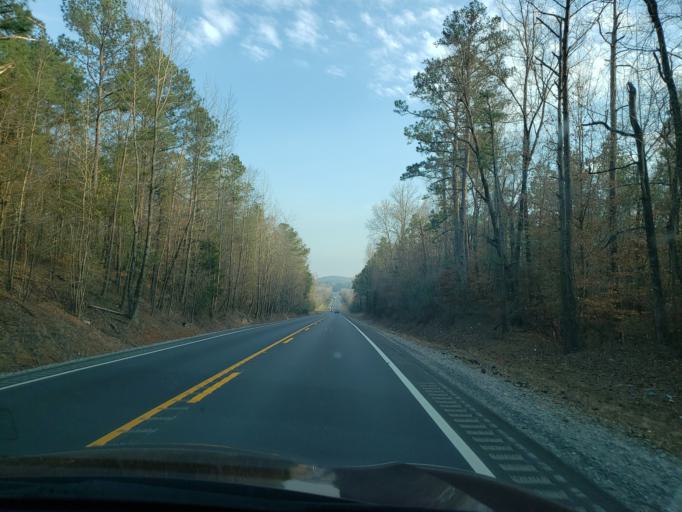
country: US
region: Alabama
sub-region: Hale County
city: Greensboro
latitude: 32.8375
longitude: -87.6075
